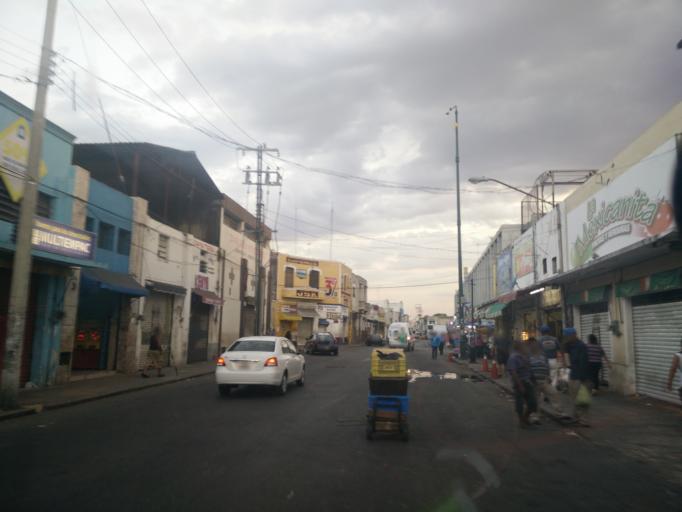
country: MX
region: Yucatan
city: Merida
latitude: 20.9633
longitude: -89.6198
